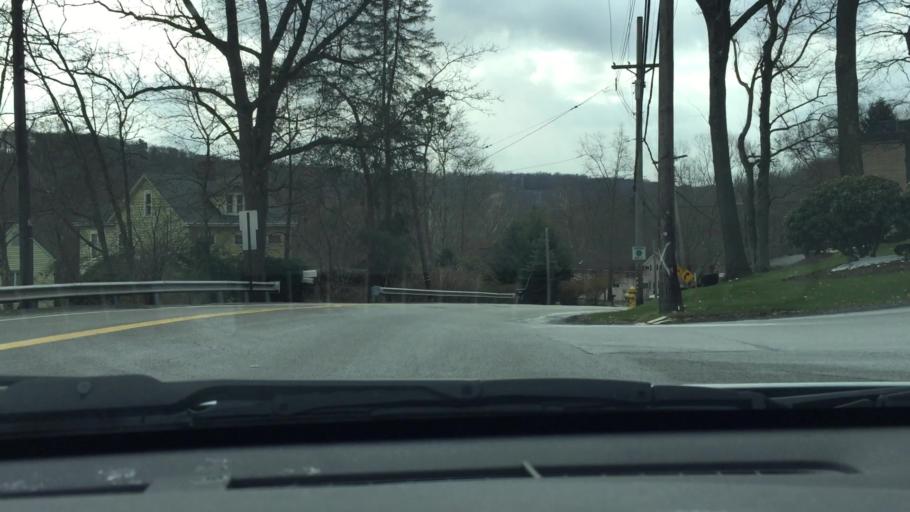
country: US
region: Pennsylvania
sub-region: Allegheny County
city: Allison Park
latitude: 40.5630
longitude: -79.9663
